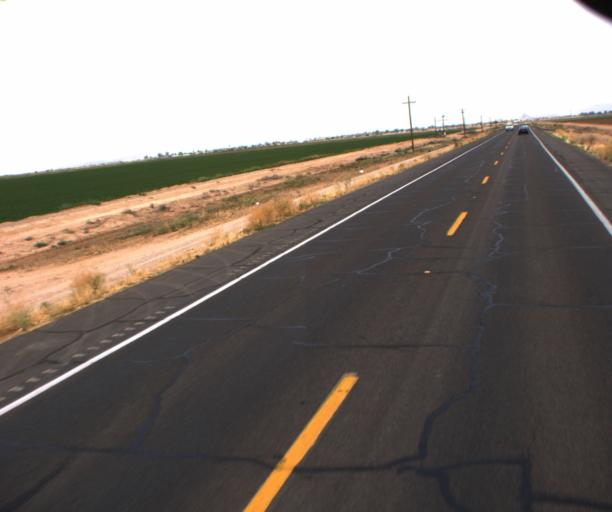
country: US
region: Arizona
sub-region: Pinal County
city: Coolidge
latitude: 32.9337
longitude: -111.5150
